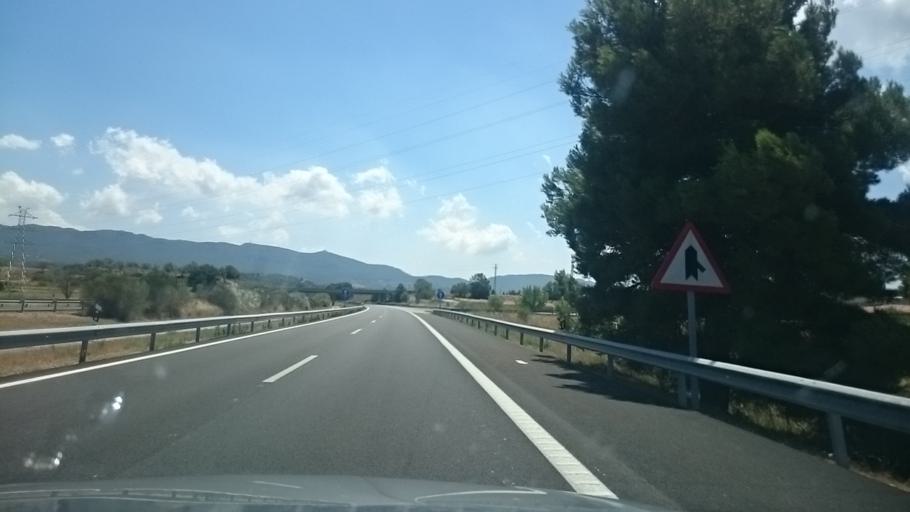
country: ES
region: Catalonia
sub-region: Provincia de Tarragona
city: Montblanc
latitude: 41.3926
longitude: 1.1645
